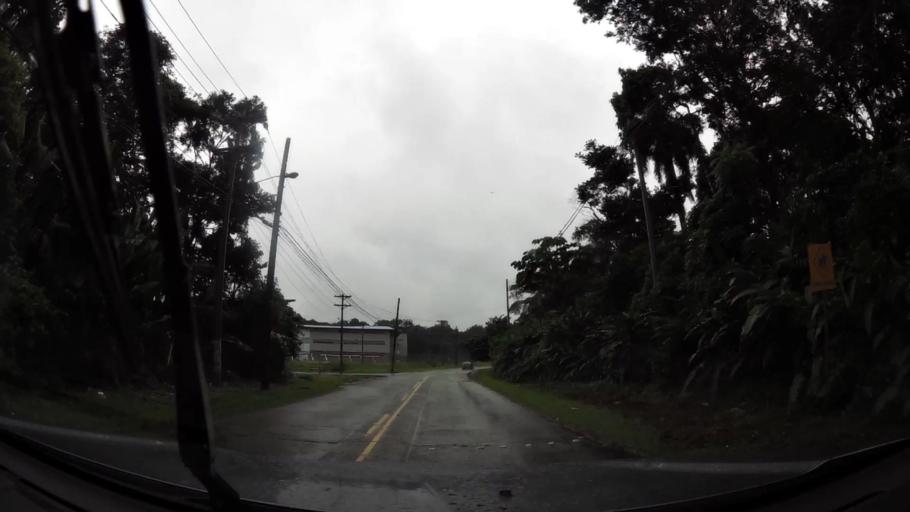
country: PA
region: Colon
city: Las Margaritas
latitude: 9.3227
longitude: -79.8867
